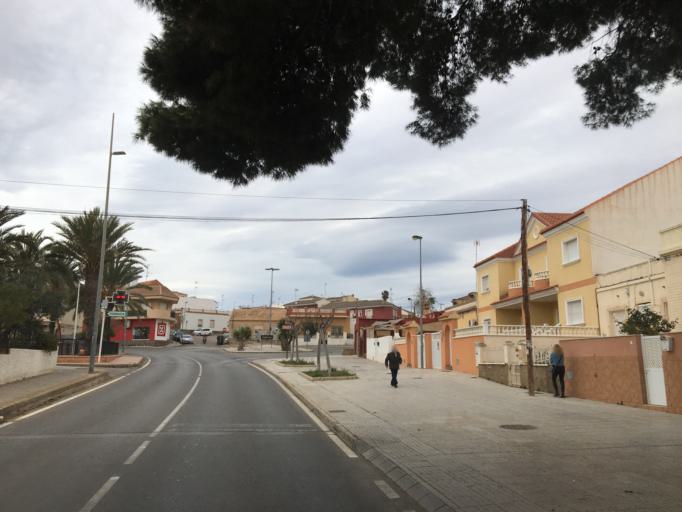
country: ES
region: Murcia
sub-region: Murcia
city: Cartagena
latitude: 37.6124
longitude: -1.0395
